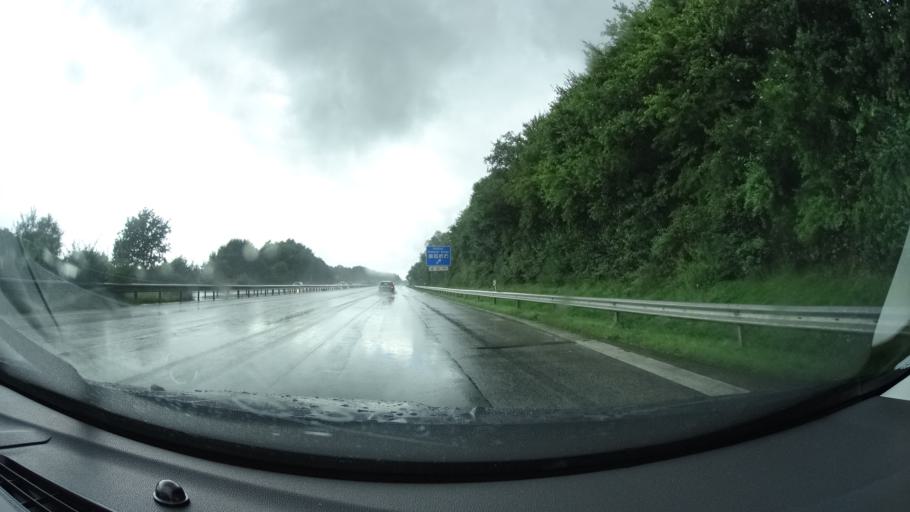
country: DE
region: Schleswig-Holstein
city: Neu Duvenstedt
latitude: 54.3609
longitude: 9.6763
